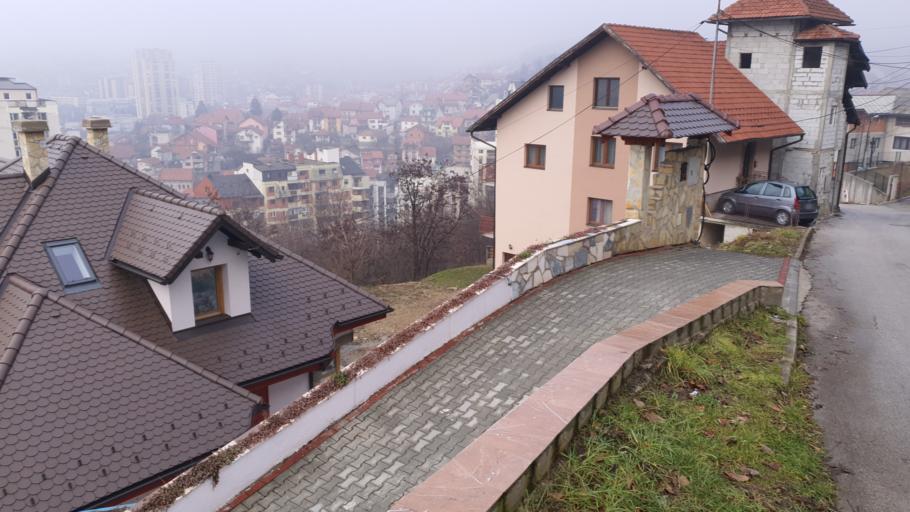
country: RS
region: Central Serbia
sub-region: Zlatiborski Okrug
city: Uzice
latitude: 43.8556
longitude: 19.8485
